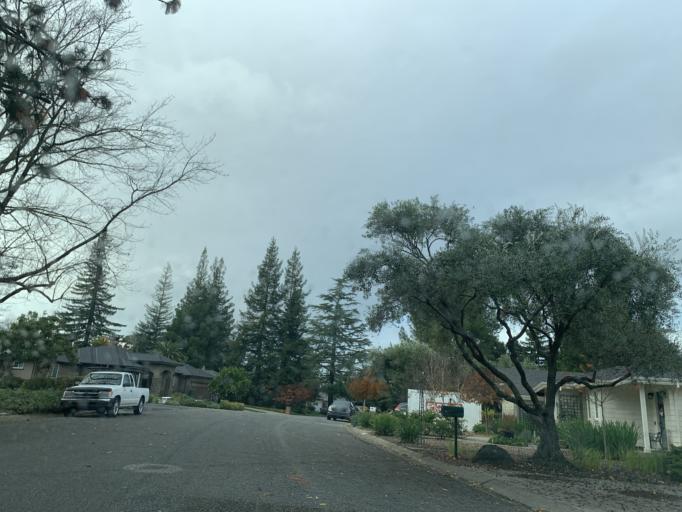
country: US
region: California
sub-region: Santa Clara County
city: Monte Sereno
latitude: 37.2667
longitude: -121.9915
